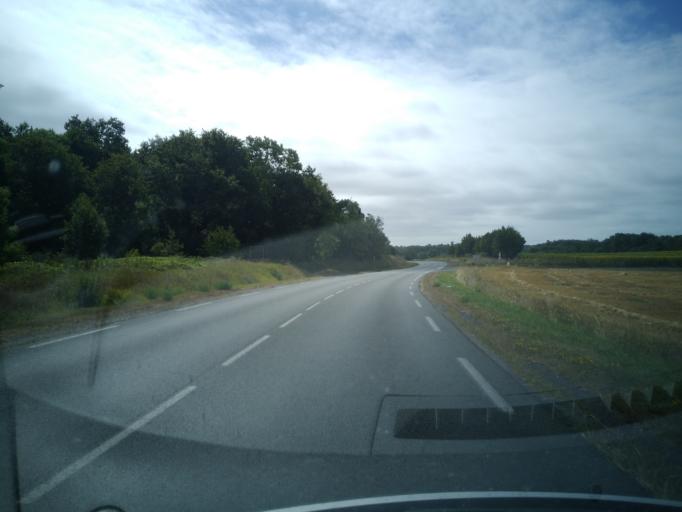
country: FR
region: Poitou-Charentes
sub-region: Departement de la Charente-Maritime
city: Breuillet
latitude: 45.7072
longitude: -1.0610
